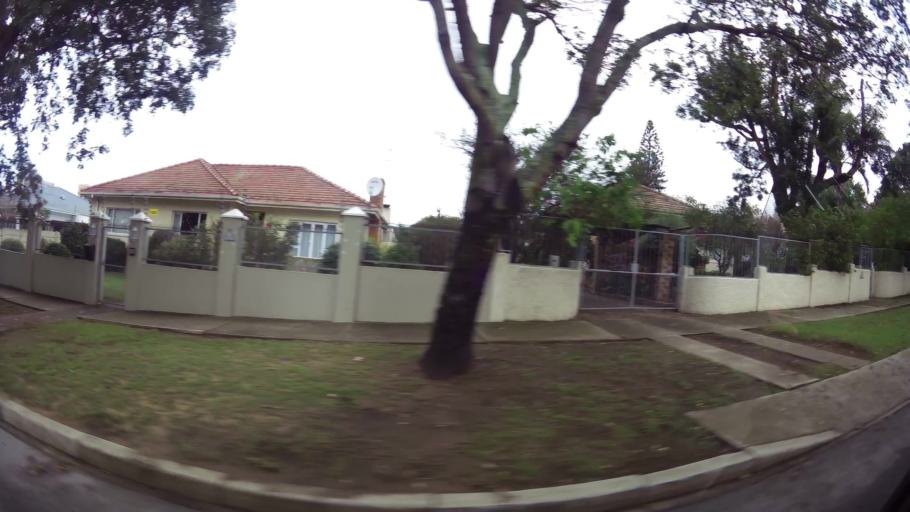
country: ZA
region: Eastern Cape
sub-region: Nelson Mandela Bay Metropolitan Municipality
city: Port Elizabeth
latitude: -33.9517
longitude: 25.5950
